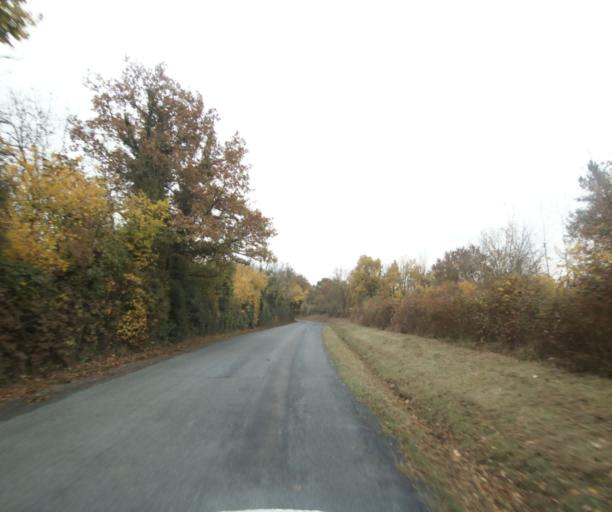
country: FR
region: Poitou-Charentes
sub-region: Departement de la Charente-Maritime
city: Saintes
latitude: 45.7372
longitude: -0.6654
